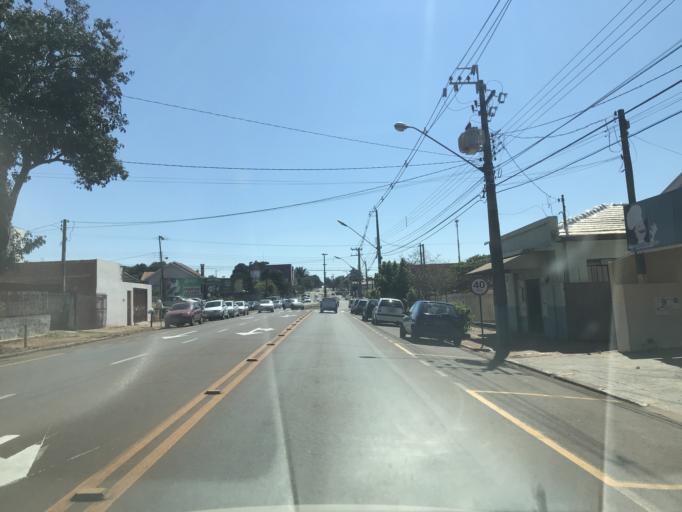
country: BR
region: Parana
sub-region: Toledo
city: Toledo
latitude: -24.7306
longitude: -53.7360
